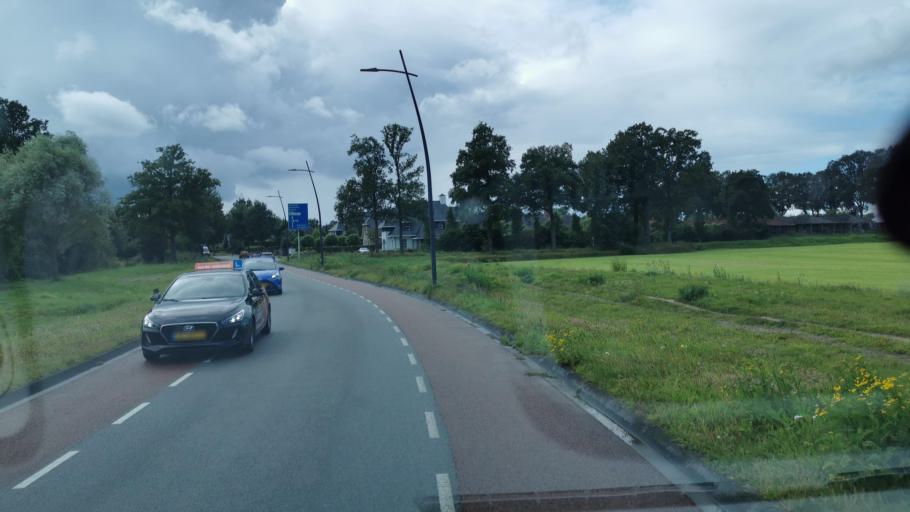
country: NL
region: Overijssel
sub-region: Gemeente Losser
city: Losser
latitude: 52.2695
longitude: 6.9946
